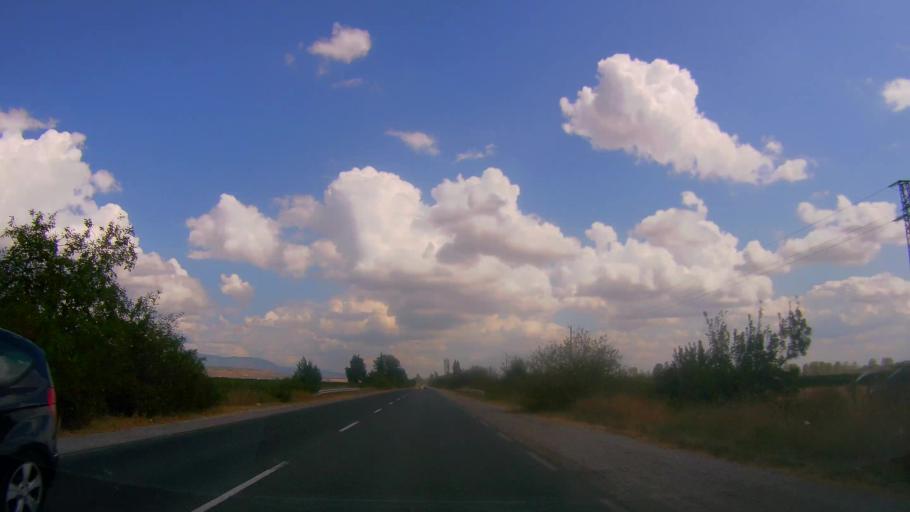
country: BG
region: Sliven
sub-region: Obshtina Sliven
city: Sliven
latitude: 42.6367
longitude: 26.2345
